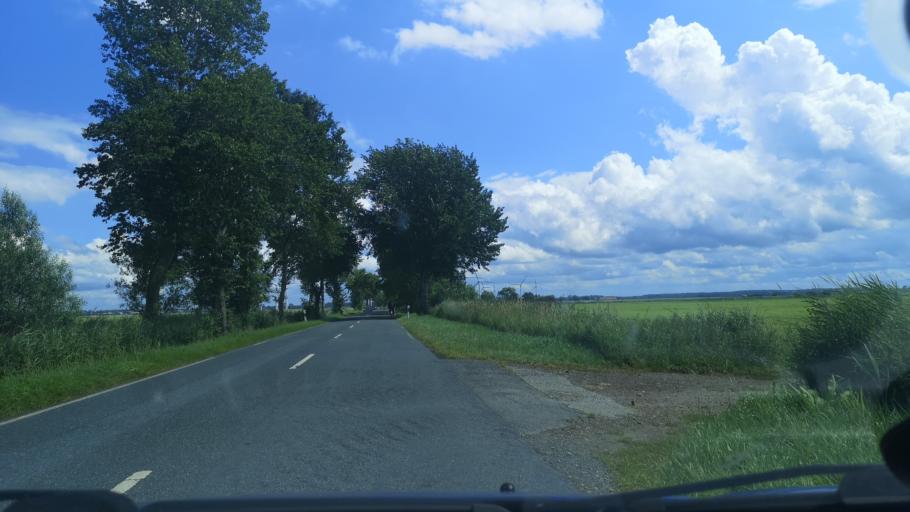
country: DE
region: Lower Saxony
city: Mulsum
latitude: 53.6466
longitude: 8.5393
